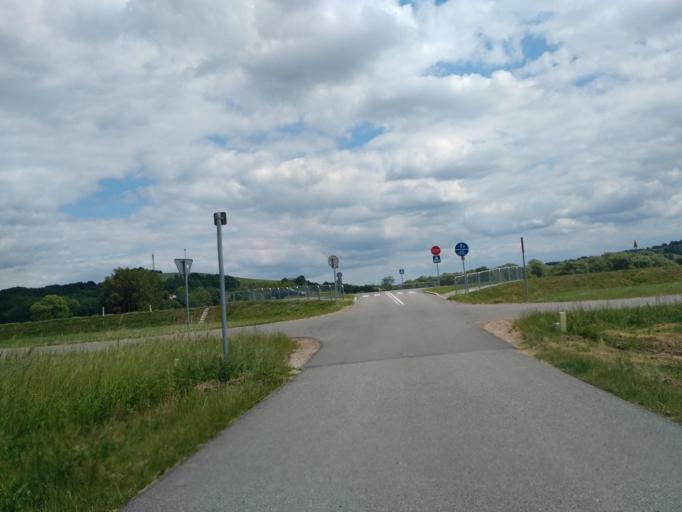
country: PL
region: Subcarpathian Voivodeship
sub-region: Powiat rzeszowski
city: Dynow
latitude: 49.8148
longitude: 22.2395
